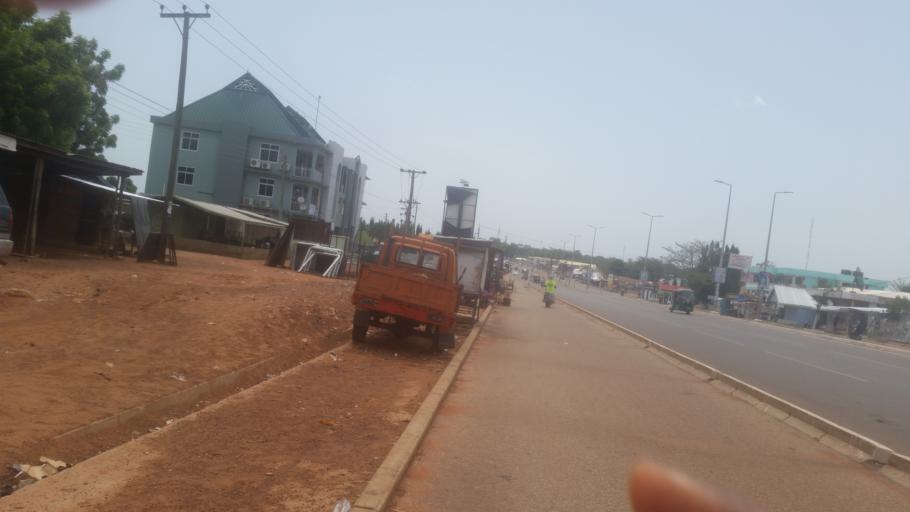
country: GH
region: Northern
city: Tamale
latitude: 9.3961
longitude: -0.8264
